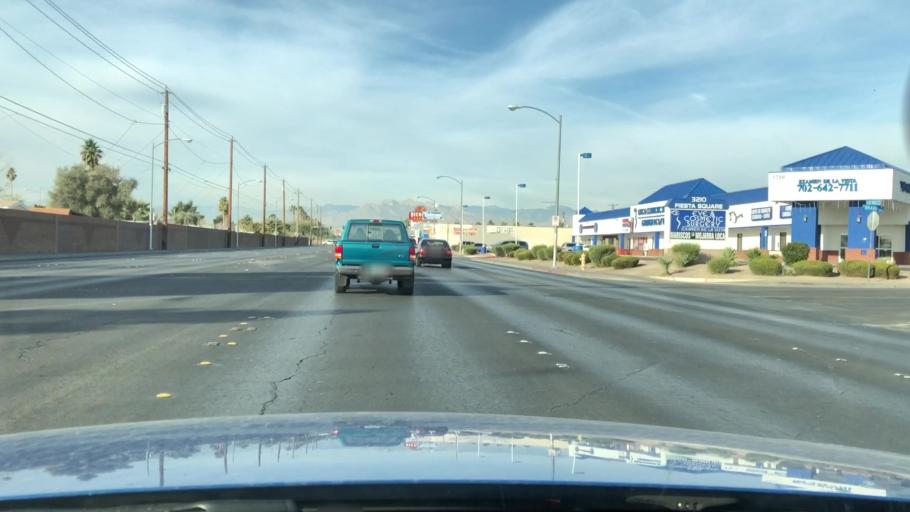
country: US
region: Nevada
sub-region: Clark County
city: North Las Vegas
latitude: 36.1959
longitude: -115.1038
